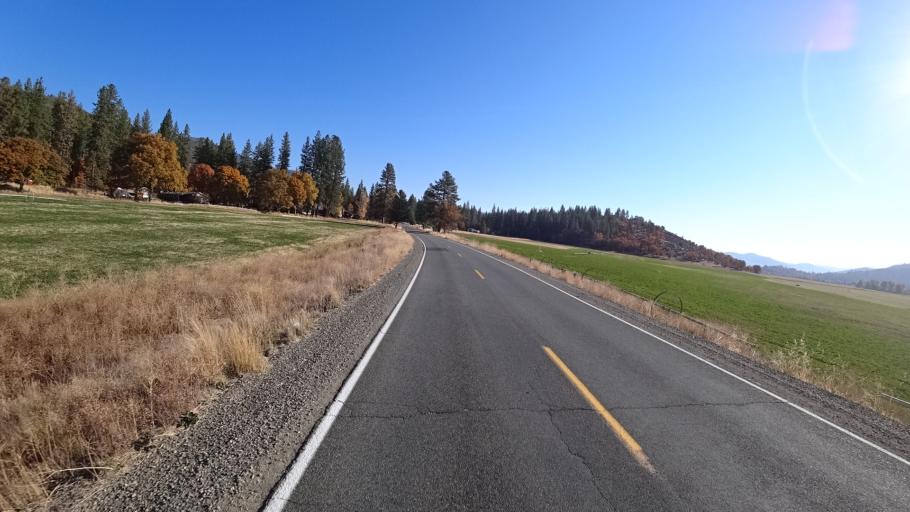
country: US
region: California
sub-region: Siskiyou County
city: Yreka
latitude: 41.6350
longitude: -122.9424
